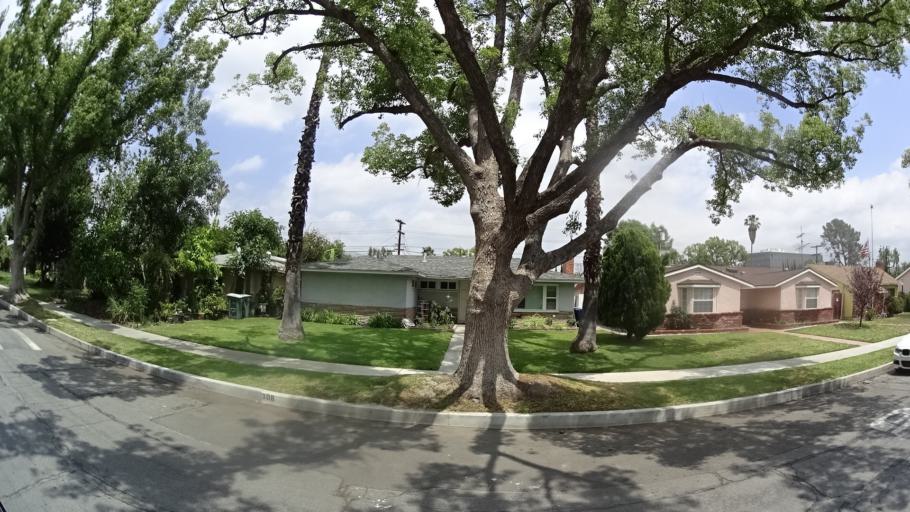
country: US
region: California
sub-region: Los Angeles County
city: Universal City
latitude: 34.1610
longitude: -118.3343
